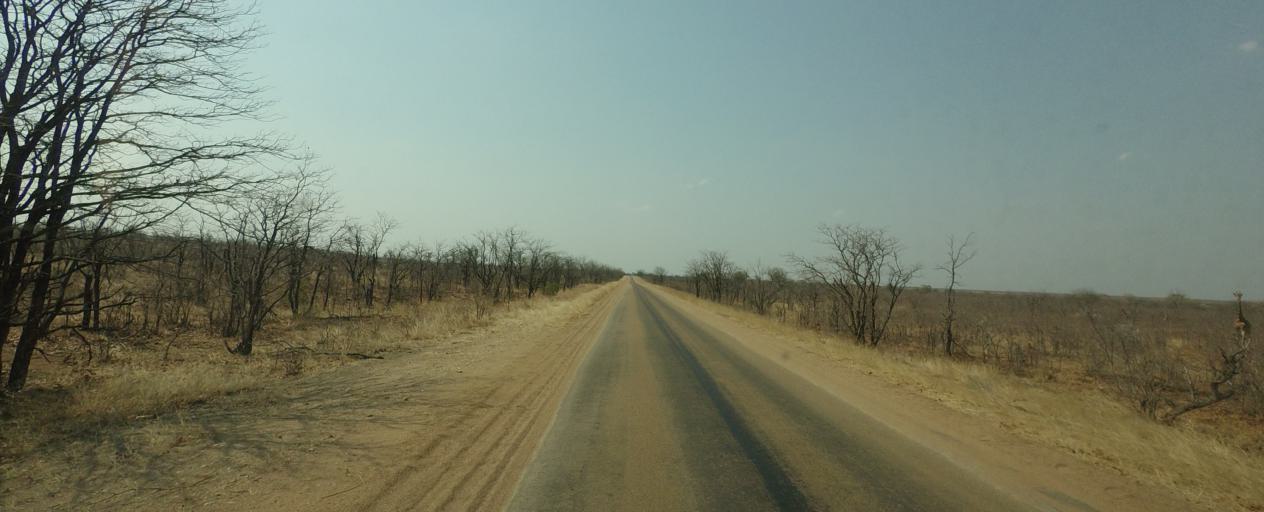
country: ZA
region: Limpopo
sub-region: Mopani District Municipality
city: Giyani
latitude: -23.2250
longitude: 31.3150
